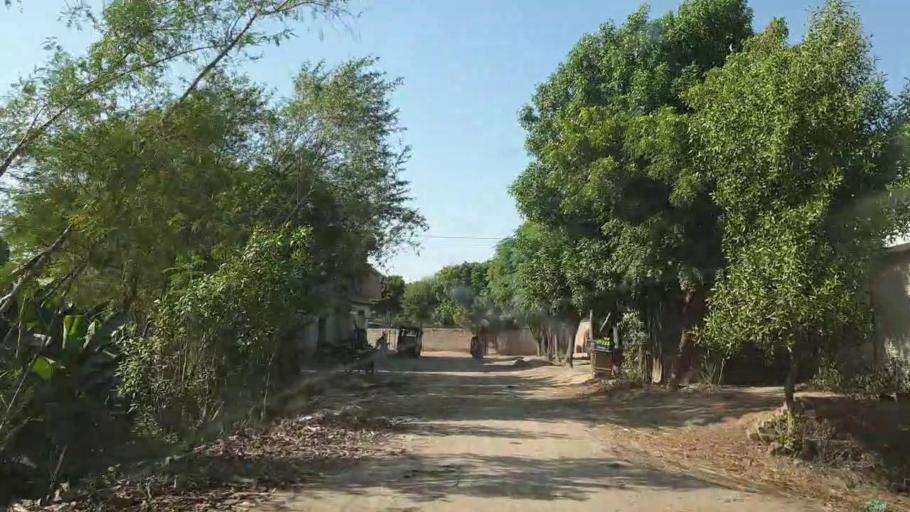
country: PK
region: Sindh
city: Tando Jam
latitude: 25.3488
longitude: 68.5813
